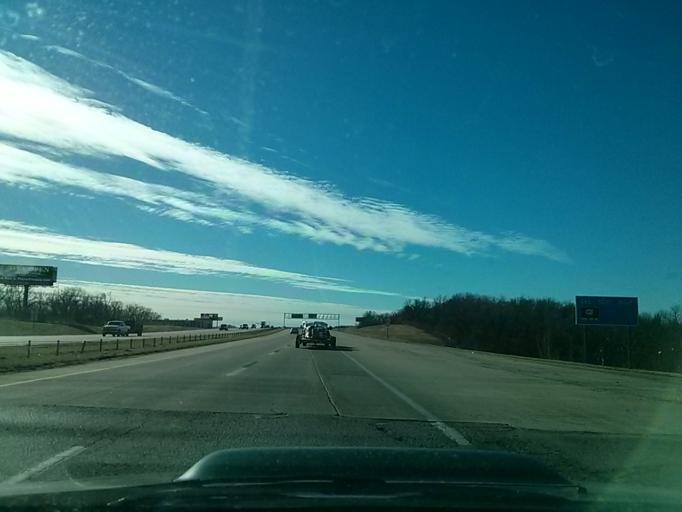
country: US
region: Oklahoma
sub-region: Tulsa County
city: Oakhurst
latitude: 36.0698
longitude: -96.0068
